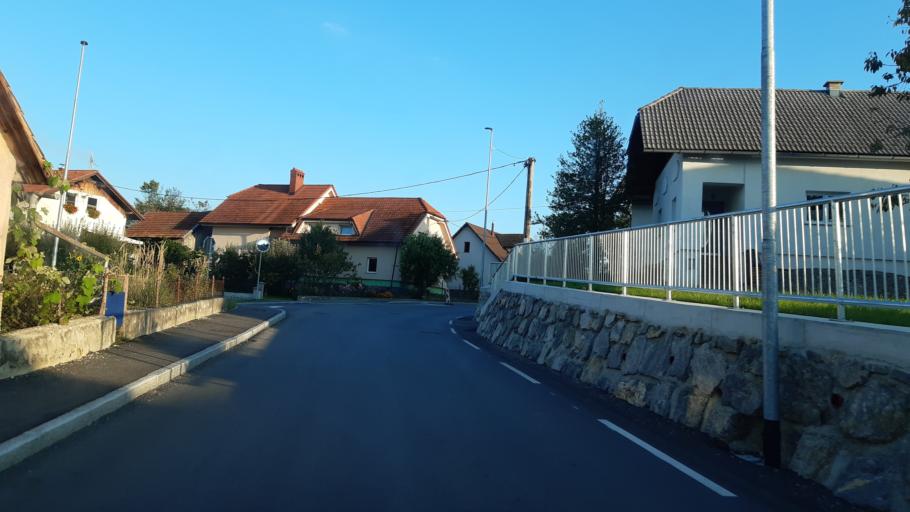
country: SI
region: Kocevje
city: Kocevje
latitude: 45.6482
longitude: 14.8802
